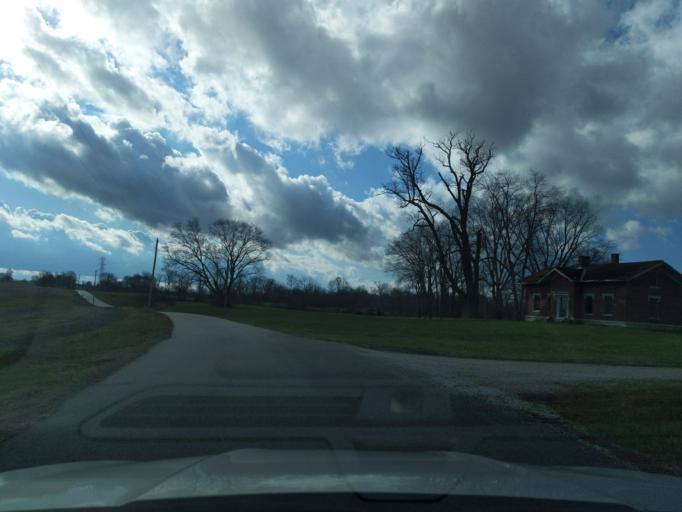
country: US
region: Indiana
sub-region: Decatur County
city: Greensburg
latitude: 39.3994
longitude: -85.5095
